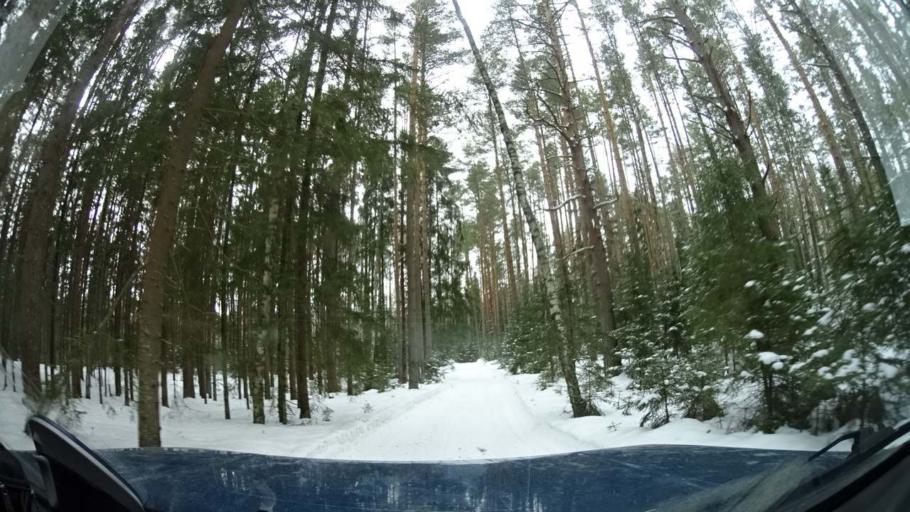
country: RU
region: Tverskaya
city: Radchenko
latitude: 56.6931
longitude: 36.4269
